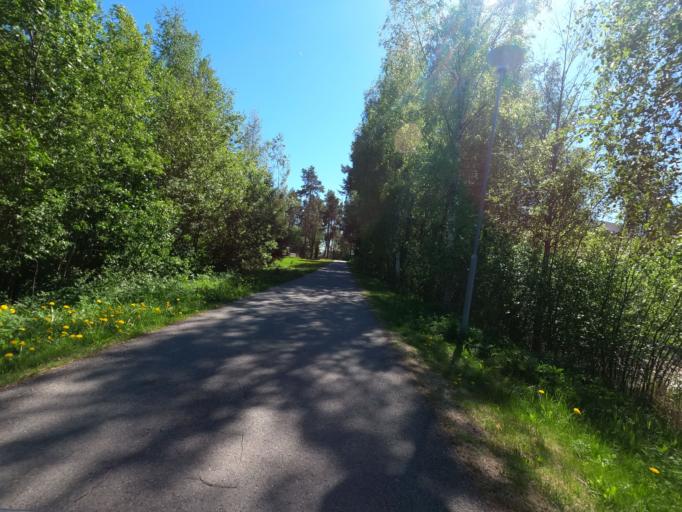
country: FI
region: North Karelia
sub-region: Joensuu
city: Joensuu
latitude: 62.5788
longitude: 29.7660
